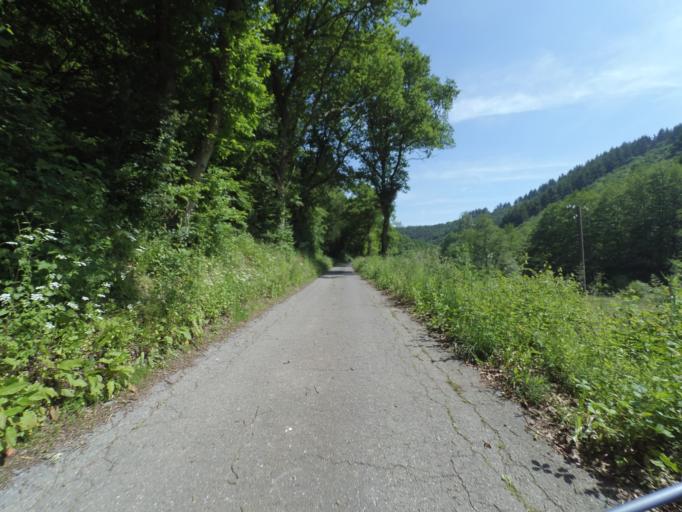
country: DE
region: Rheinland-Pfalz
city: Reudelsterz
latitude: 50.2892
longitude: 7.1373
